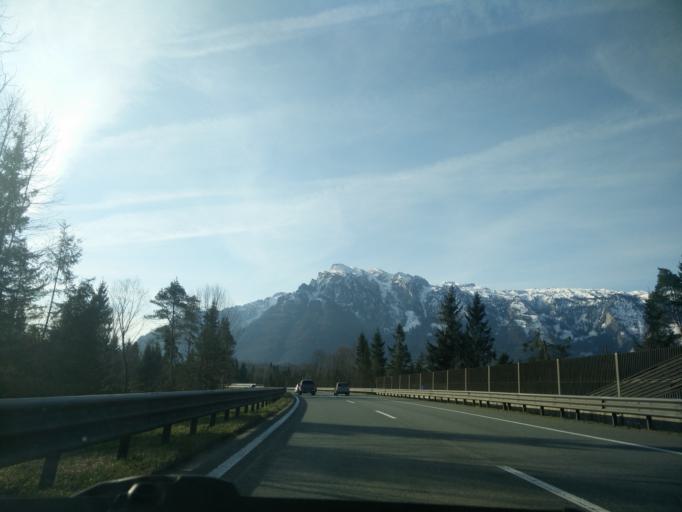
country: DE
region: Bavaria
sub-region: Upper Bavaria
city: Ainring
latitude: 47.7733
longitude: 12.9794
